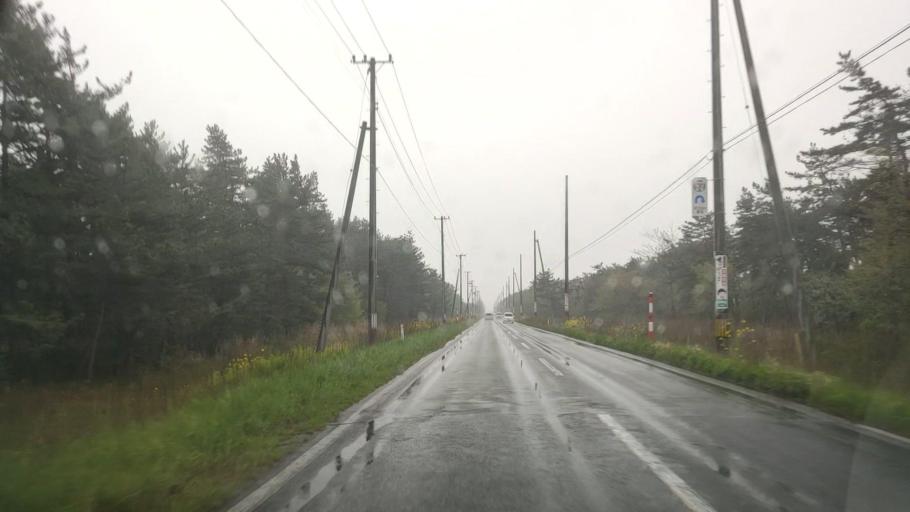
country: JP
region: Akita
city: Tenno
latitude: 40.0094
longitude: 139.9513
